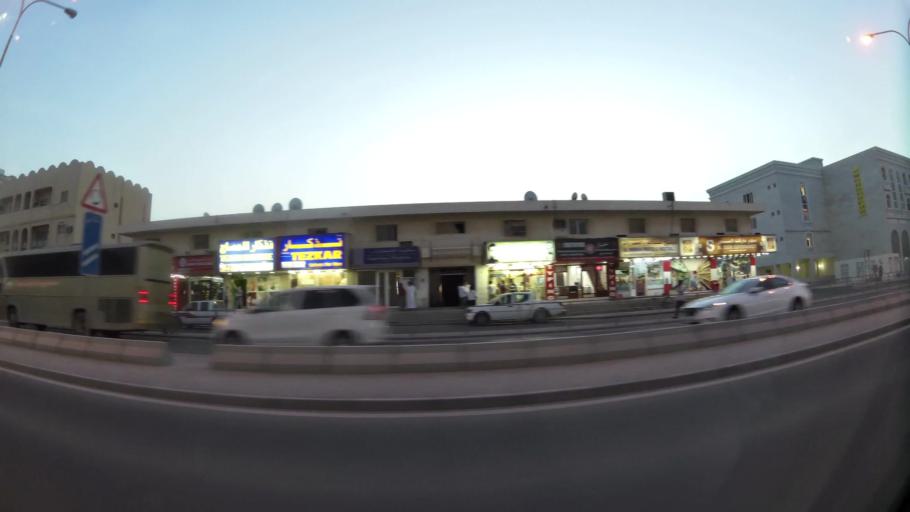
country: QA
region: Al Wakrah
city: Al Wakrah
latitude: 25.1631
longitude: 51.5979
